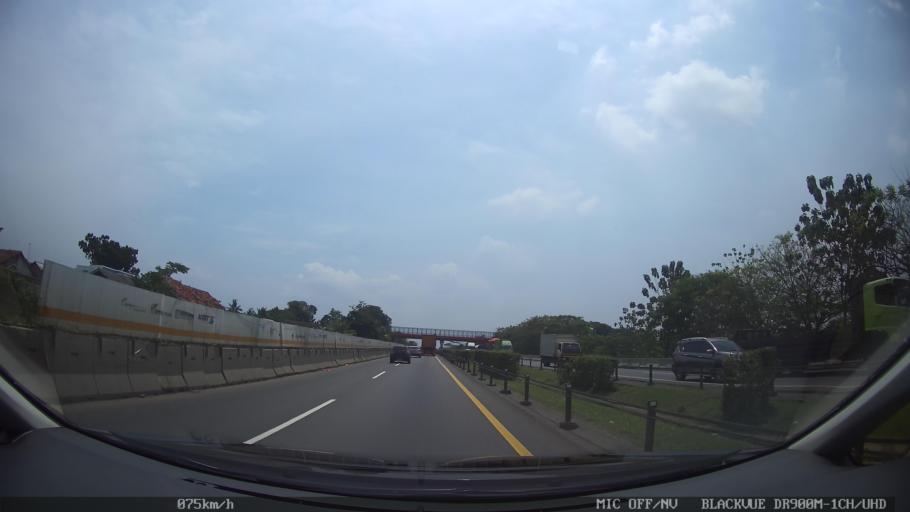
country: ID
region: West Java
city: Kresek
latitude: -6.1422
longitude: 106.2712
